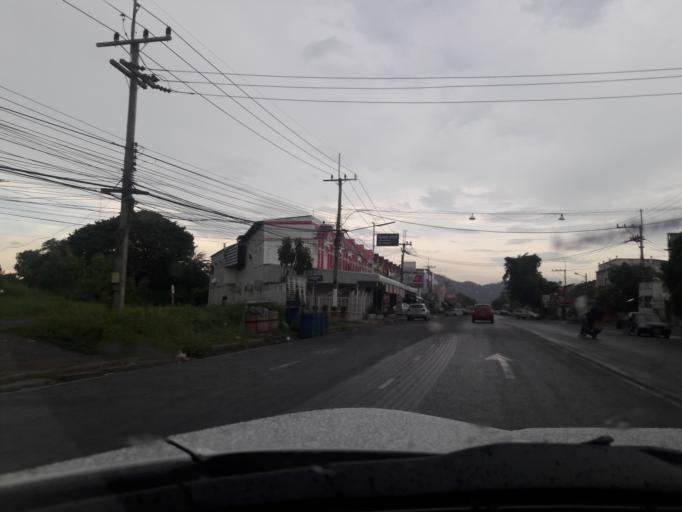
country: TH
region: Lop Buri
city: Lop Buri
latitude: 14.7893
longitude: 100.6768
